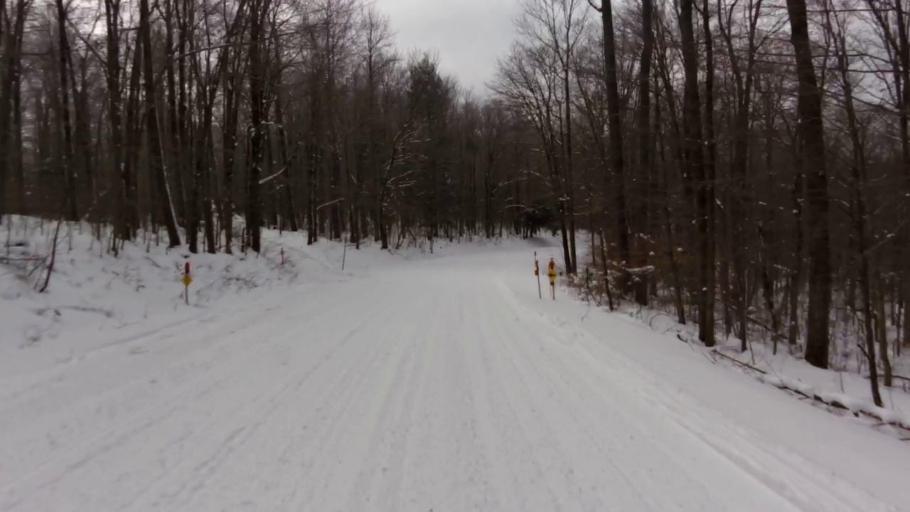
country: US
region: New York
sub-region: Cattaraugus County
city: Salamanca
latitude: 42.0414
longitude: -78.7825
